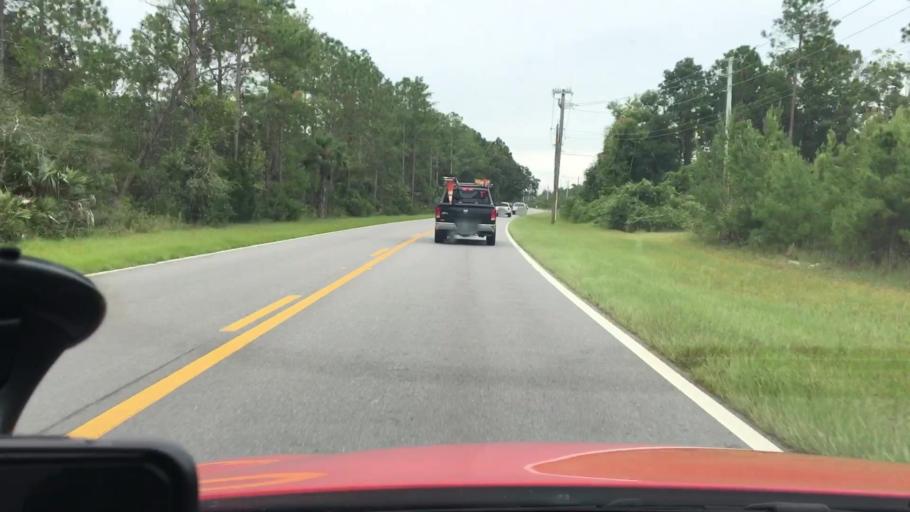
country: US
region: Florida
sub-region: Flagler County
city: Palm Coast
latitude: 29.5182
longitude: -81.1975
